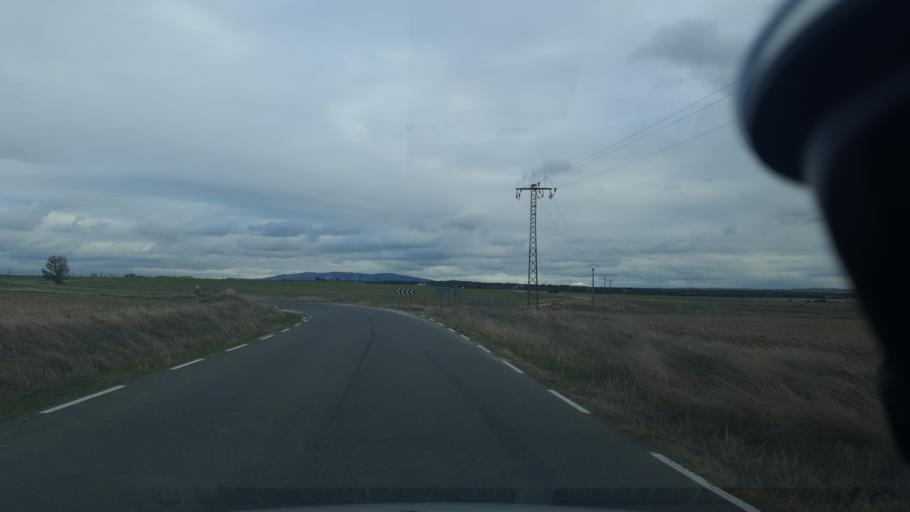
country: ES
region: Castille and Leon
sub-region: Provincia de Avila
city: Velayos
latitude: 40.8363
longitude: -4.6178
